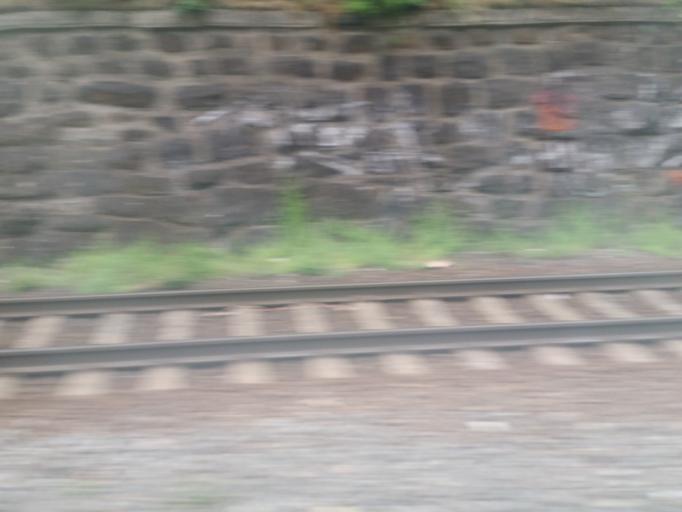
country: SK
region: Bratislavsky
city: Bratislava
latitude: 48.1637
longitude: 17.0909
